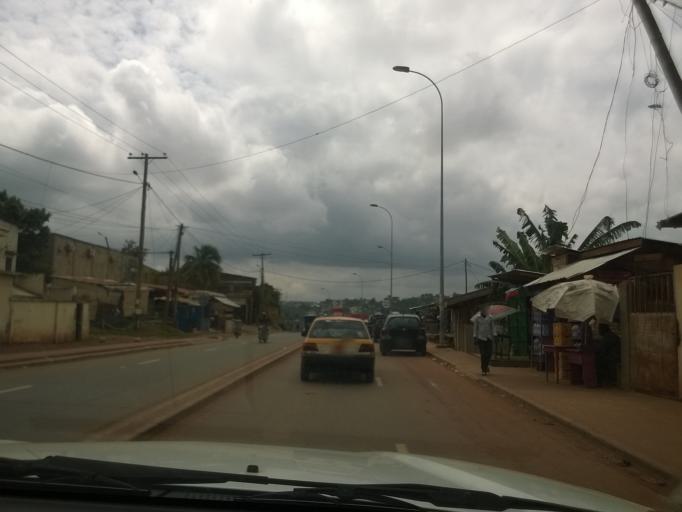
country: CM
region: Centre
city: Yaounde
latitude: 3.8333
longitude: 11.4936
